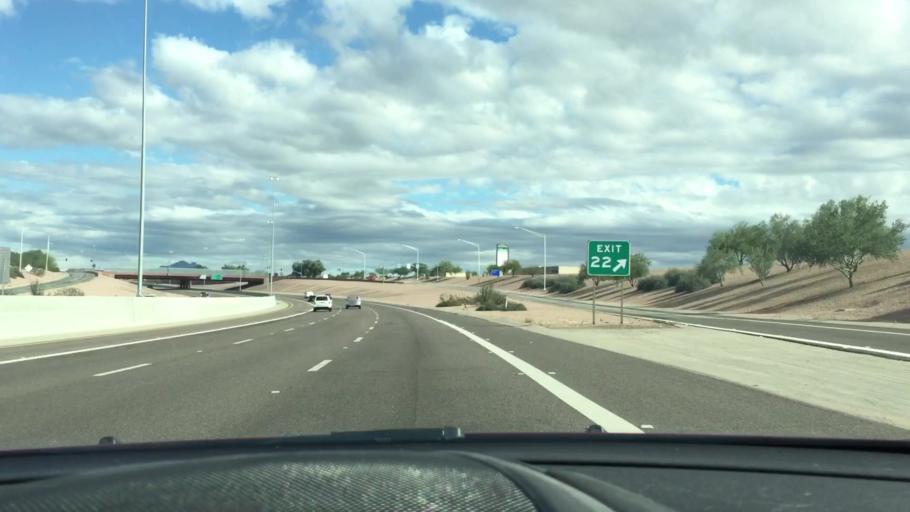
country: US
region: Arizona
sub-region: Maricopa County
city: Mesa
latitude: 33.4764
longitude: -111.7061
